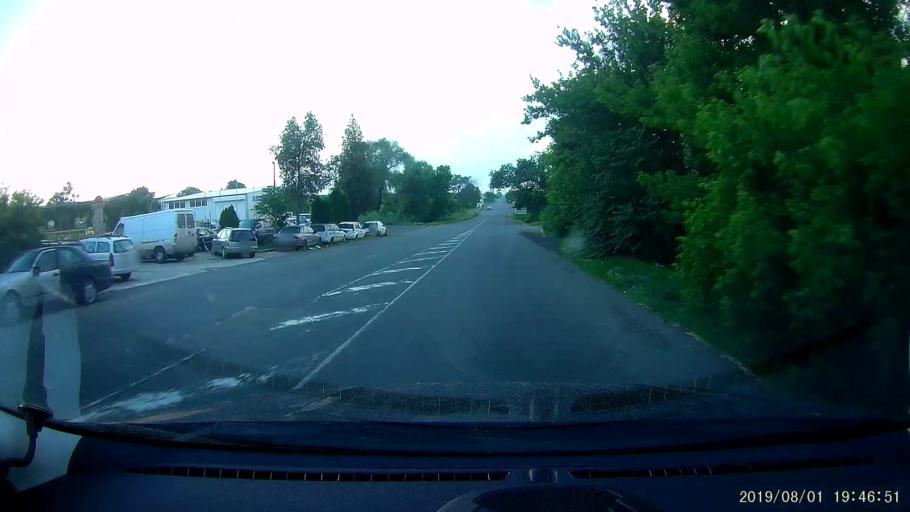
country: BG
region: Burgas
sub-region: Obshtina Karnobat
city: Karnobat
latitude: 42.6502
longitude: 26.9664
